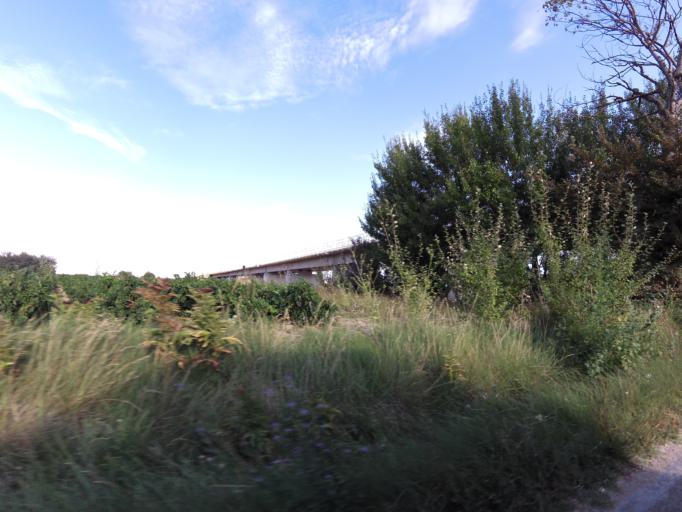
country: FR
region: Languedoc-Roussillon
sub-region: Departement du Gard
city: Gallargues-le-Montueux
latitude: 43.7038
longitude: 4.1684
